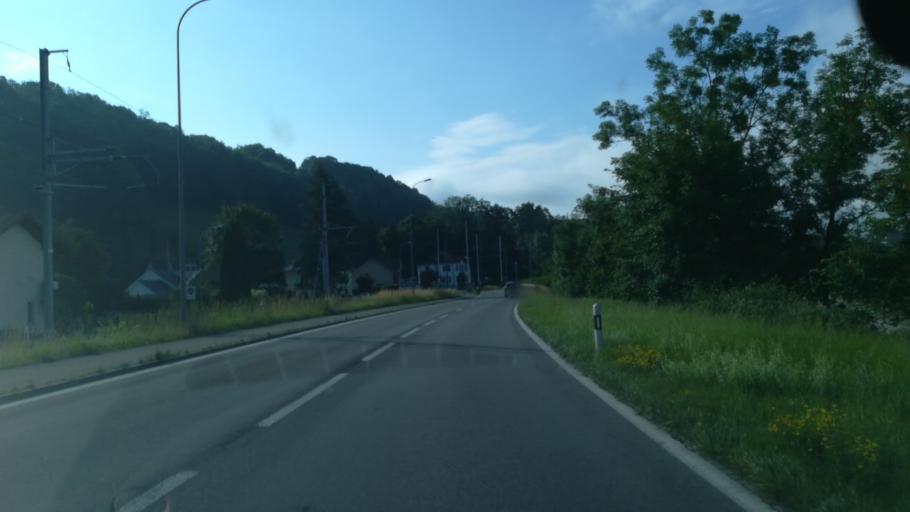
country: CH
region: Thurgau
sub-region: Weinfelden District
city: Sulgen
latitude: 47.5219
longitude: 9.2060
